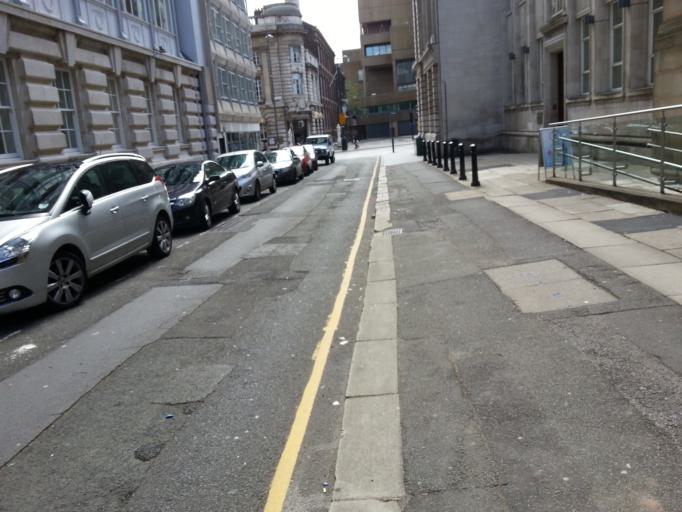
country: GB
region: England
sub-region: Liverpool
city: Liverpool
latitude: 53.4096
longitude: -2.9933
